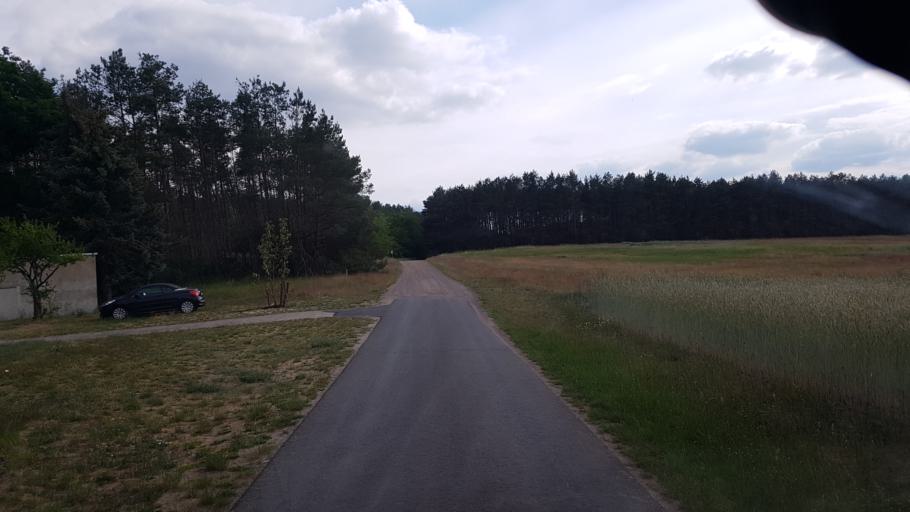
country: DE
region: Brandenburg
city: Herzberg
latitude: 51.7441
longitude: 13.2801
